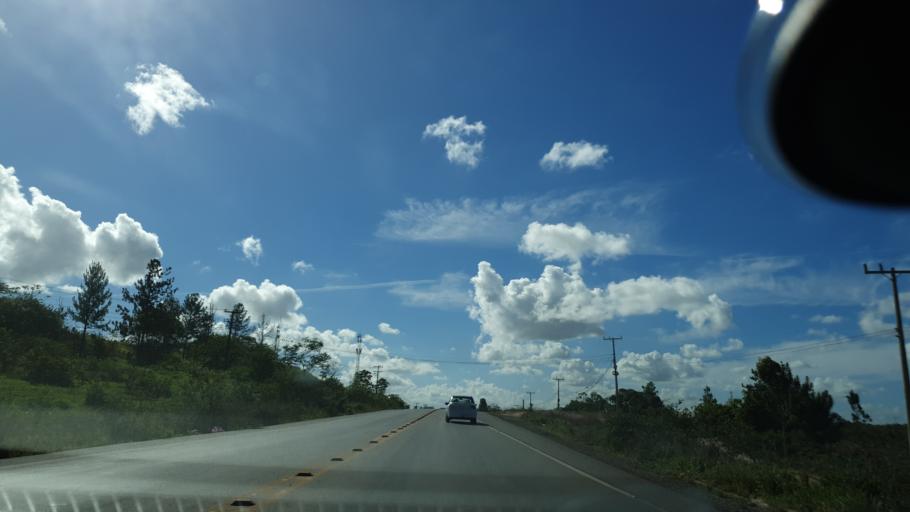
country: BR
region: Bahia
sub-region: Camacari
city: Camacari
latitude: -12.6851
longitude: -38.2728
